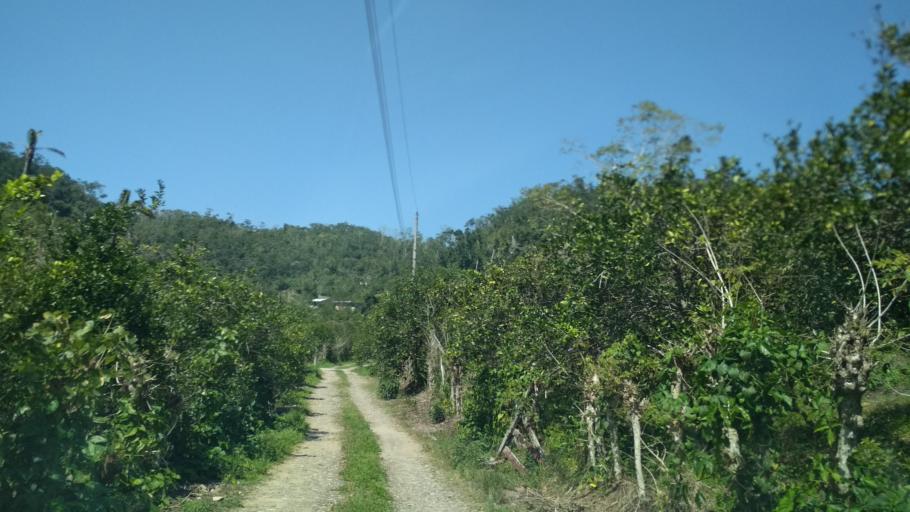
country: MX
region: Veracruz
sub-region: Papantla
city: Polutla
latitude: 20.4876
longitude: -97.2292
